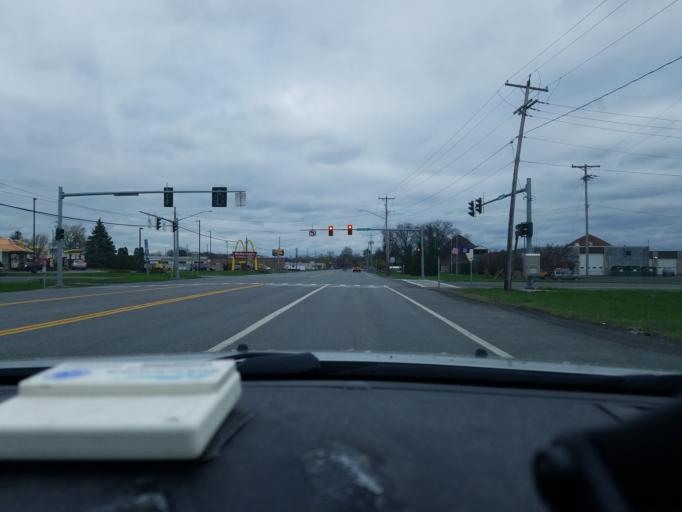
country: US
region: New York
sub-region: Onondaga County
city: Mattydale
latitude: 43.1179
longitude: -76.1427
